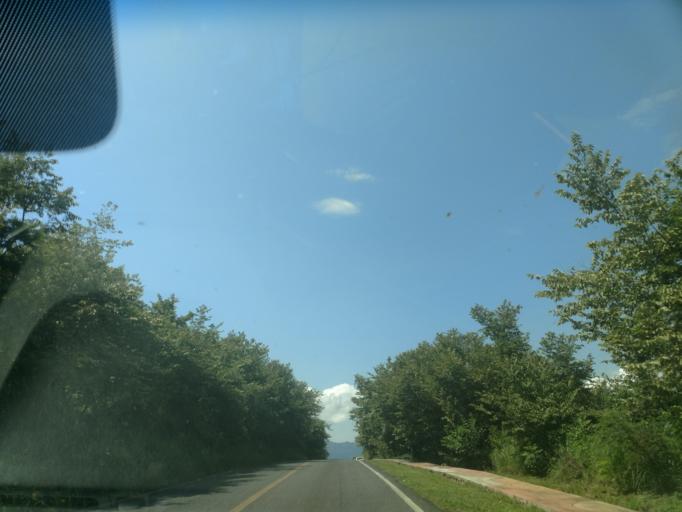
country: MX
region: Jalisco
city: Talpa de Allende
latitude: 20.4032
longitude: -104.8129
